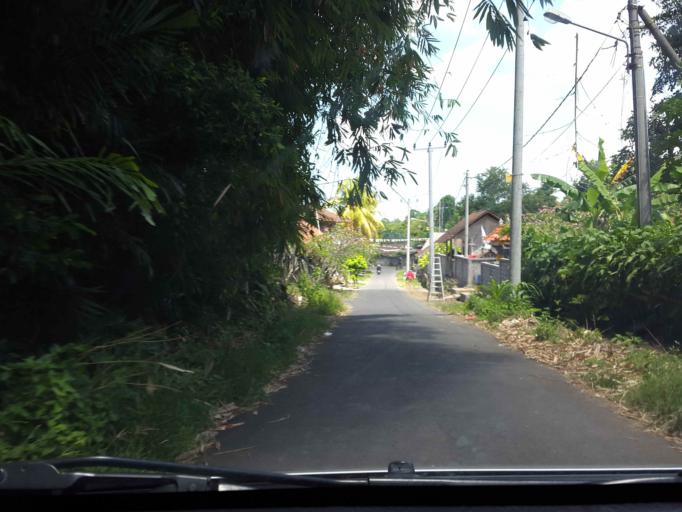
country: ID
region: Bali
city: Banjar Wangsian
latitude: -8.4964
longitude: 115.4045
